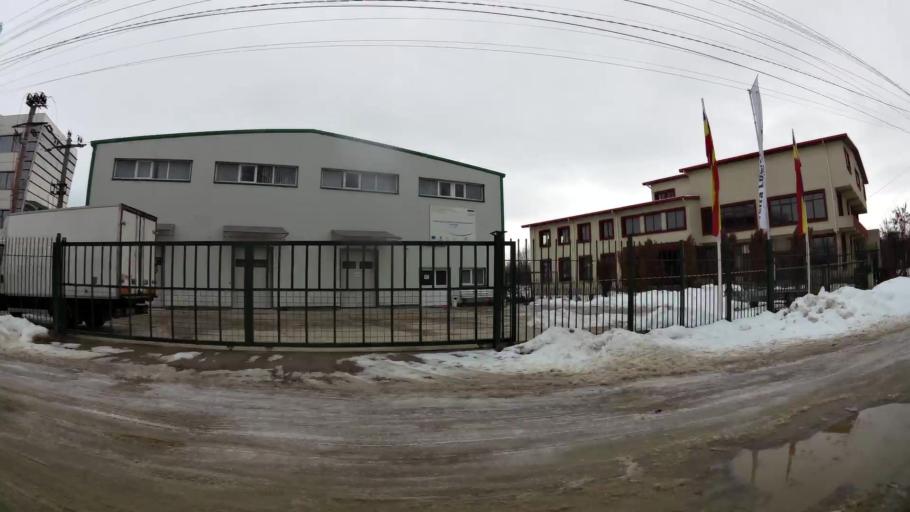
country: RO
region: Ilfov
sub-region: Comuna Pantelimon
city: Pantelimon
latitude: 44.4524
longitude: 26.2182
